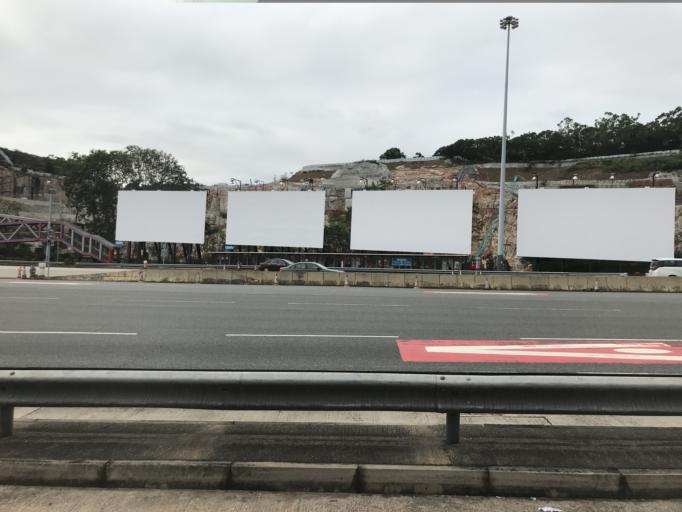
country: HK
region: Kowloon City
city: Kowloon
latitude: 22.3007
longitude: 114.2338
